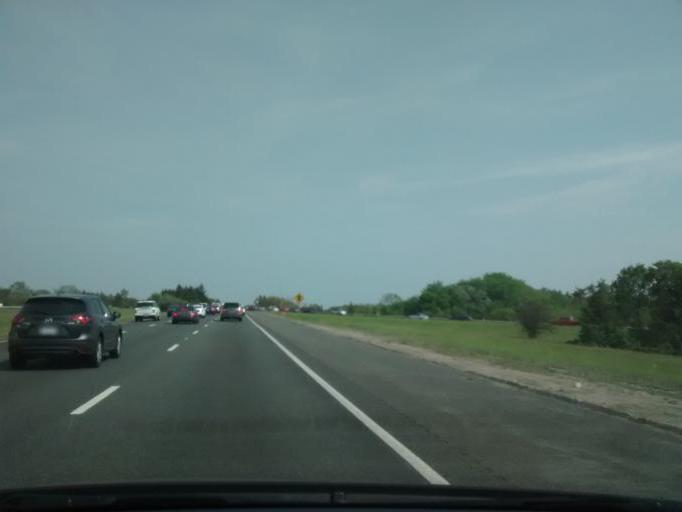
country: US
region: Massachusetts
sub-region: Bristol County
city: Raynham Center
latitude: 41.9507
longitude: -71.0273
